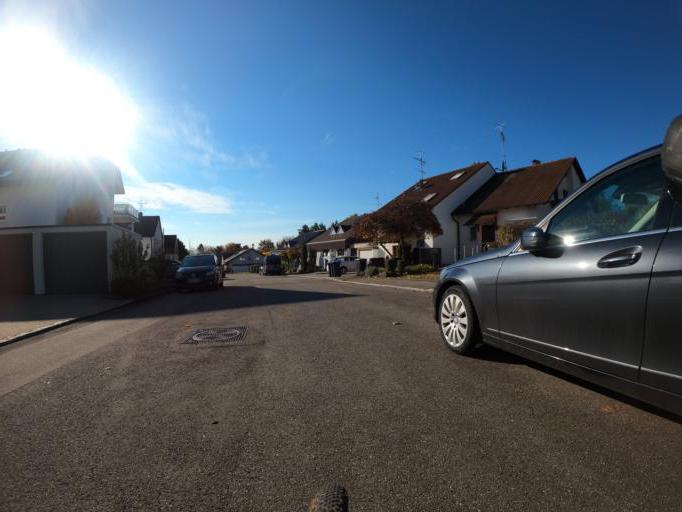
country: DE
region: Baden-Wuerttemberg
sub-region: Regierungsbezirk Stuttgart
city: Magstadt
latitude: 48.7214
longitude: 8.9588
